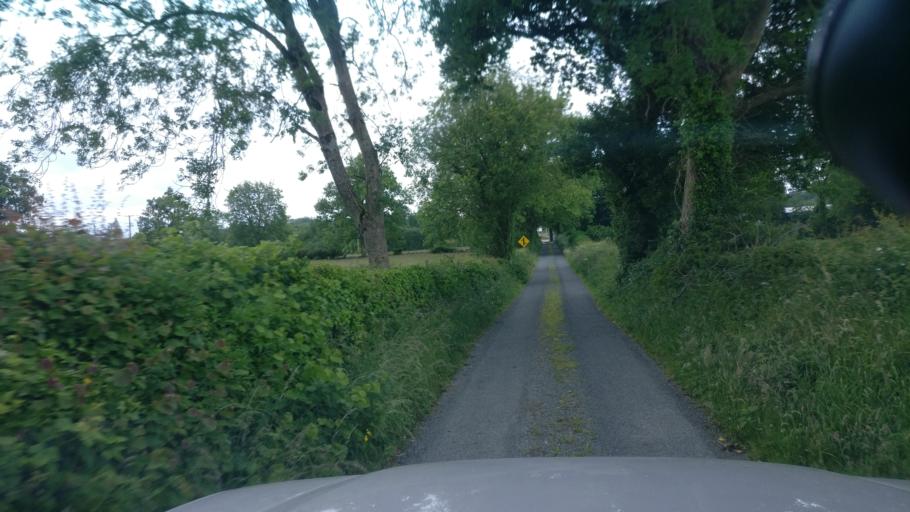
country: IE
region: Connaught
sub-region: County Galway
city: Ballinasloe
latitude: 53.3096
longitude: -8.2594
